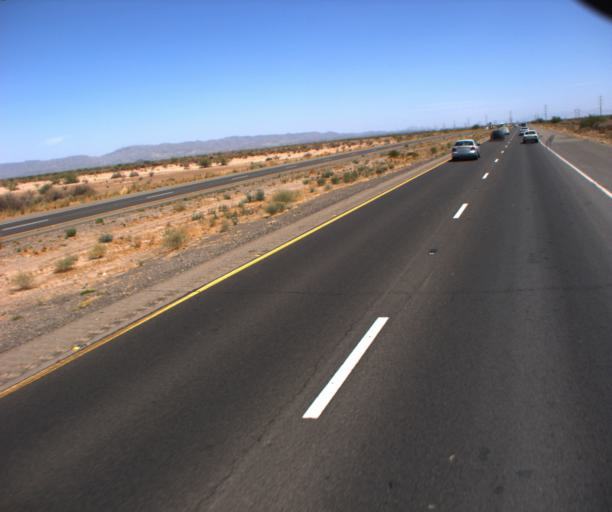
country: US
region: Arizona
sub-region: Maricopa County
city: Sun Lakes
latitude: 33.1849
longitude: -112.0000
